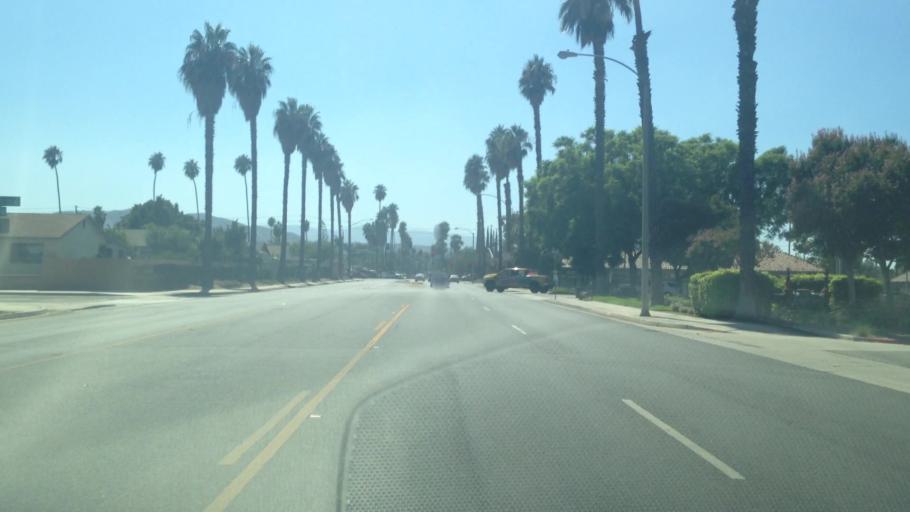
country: US
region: California
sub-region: Riverside County
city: Riverside
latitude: 33.9091
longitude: -117.4345
